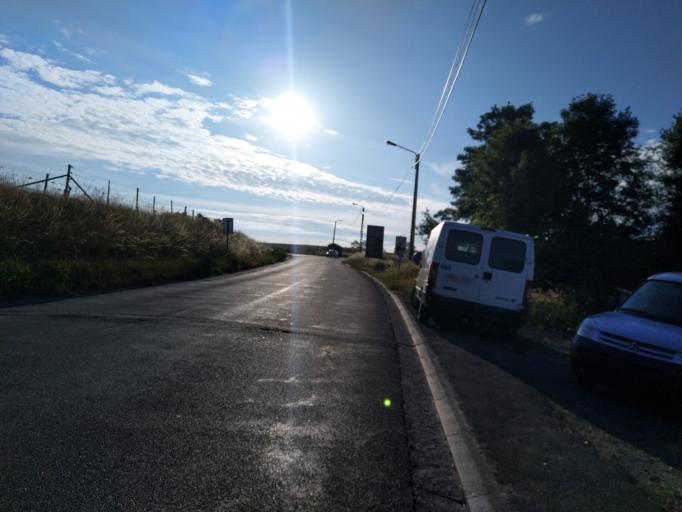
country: BE
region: Wallonia
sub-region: Province du Hainaut
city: Roeulx
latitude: 50.4735
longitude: 4.0786
